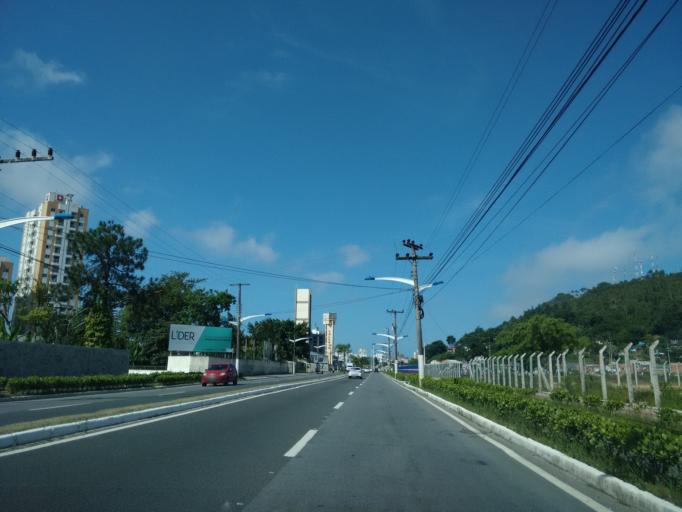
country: BR
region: Santa Catarina
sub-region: Itajai
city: Itajai
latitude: -26.9217
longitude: -48.6734
